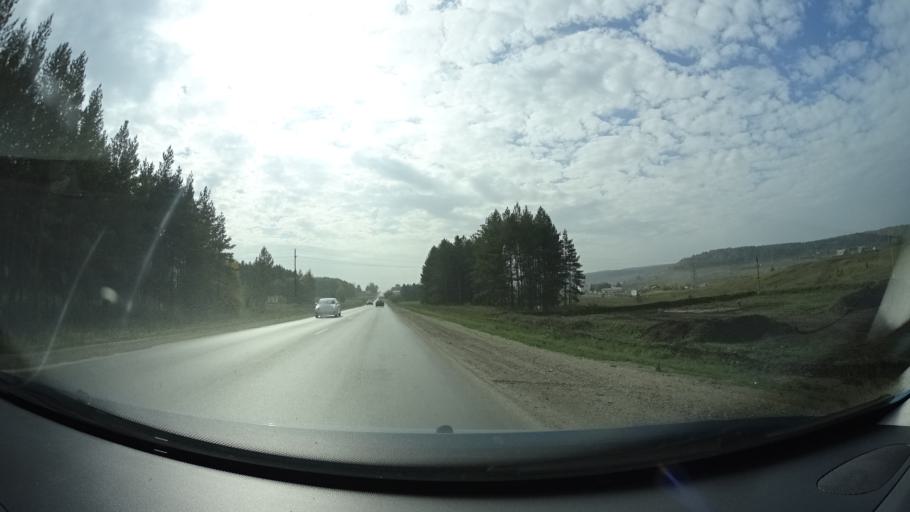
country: RU
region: Bashkortostan
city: Oktyabr'skiy
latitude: 54.5243
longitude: 53.5454
